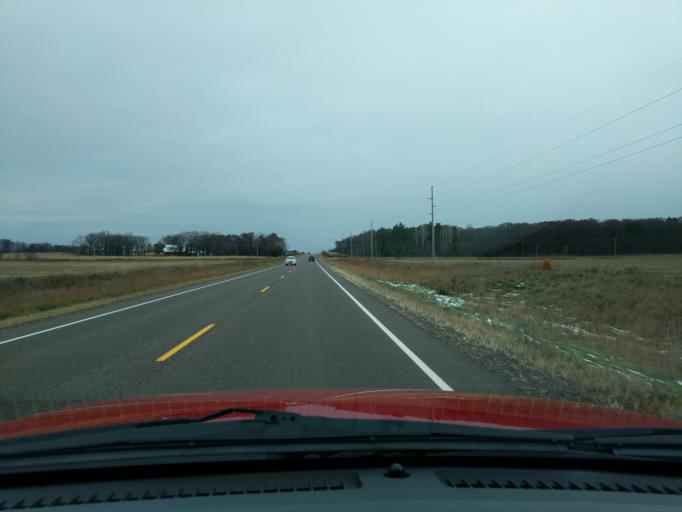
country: US
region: Wisconsin
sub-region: Washburn County
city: Shell Lake
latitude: 45.8158
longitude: -92.1097
